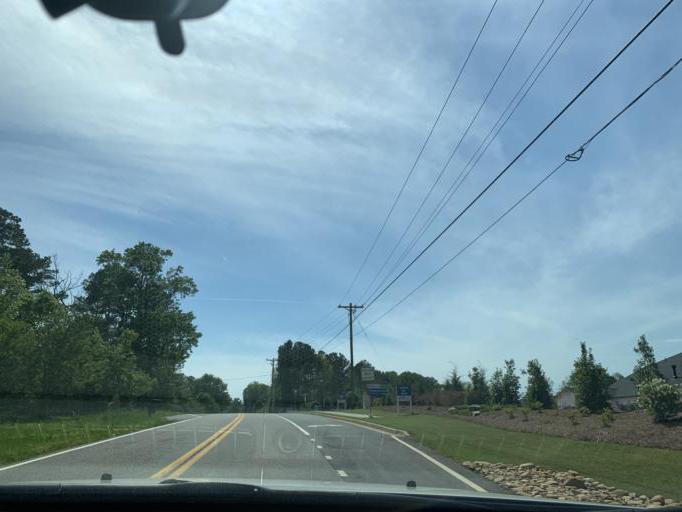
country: US
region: Georgia
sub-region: Forsyth County
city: Cumming
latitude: 34.2634
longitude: -84.1888
